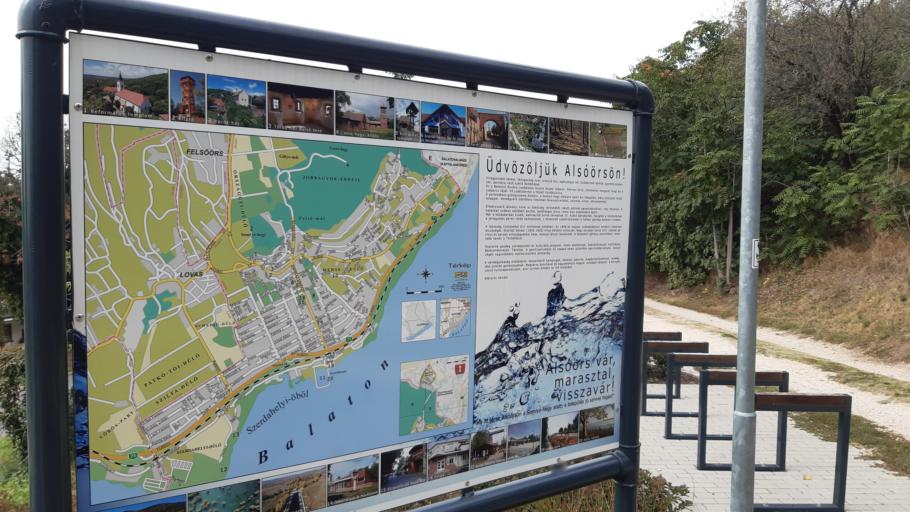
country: HU
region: Veszprem
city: Csopak
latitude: 46.9950
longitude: 17.9681
